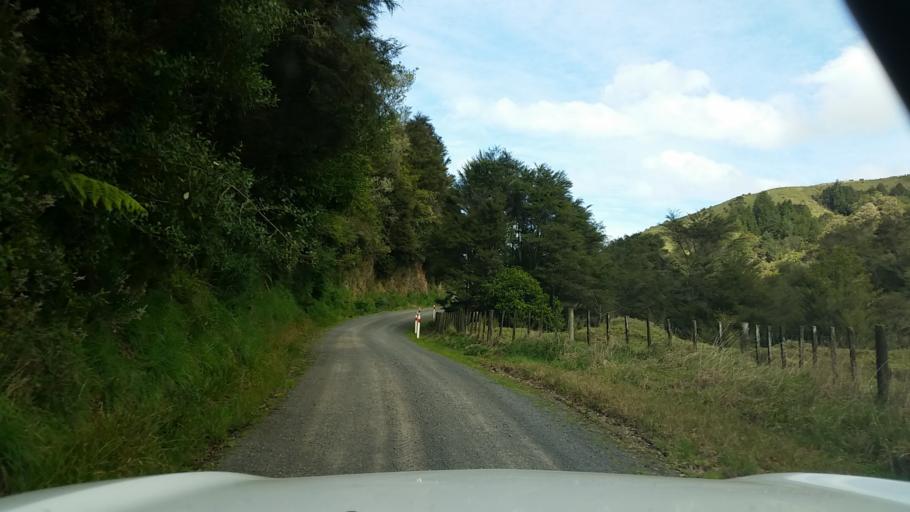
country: NZ
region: Waikato
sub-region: Hauraki District
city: Ngatea
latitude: -37.4712
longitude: 175.4572
